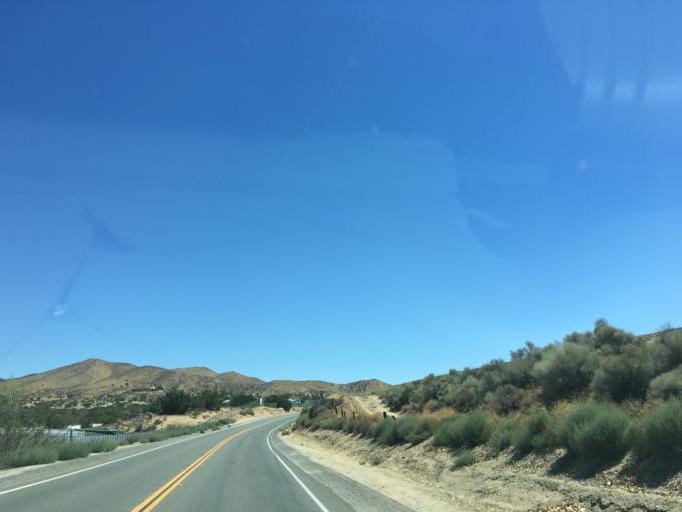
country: US
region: California
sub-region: Los Angeles County
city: Acton
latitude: 34.4701
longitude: -118.1922
